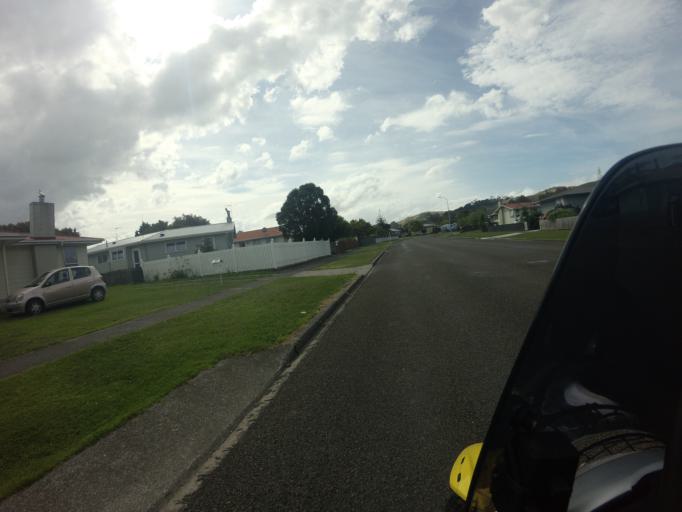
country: NZ
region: Gisborne
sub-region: Gisborne District
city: Gisborne
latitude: -38.6773
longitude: 178.0551
